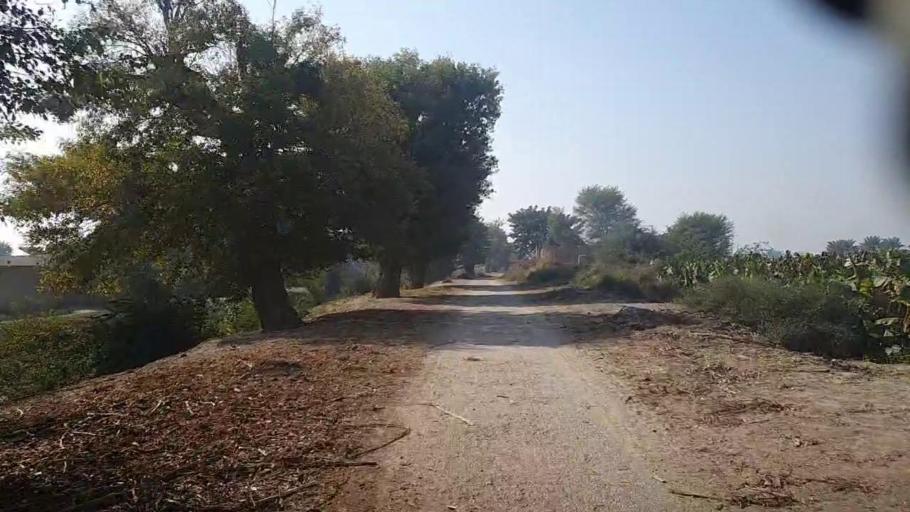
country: PK
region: Sindh
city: Kandiari
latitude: 27.0073
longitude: 68.4963
